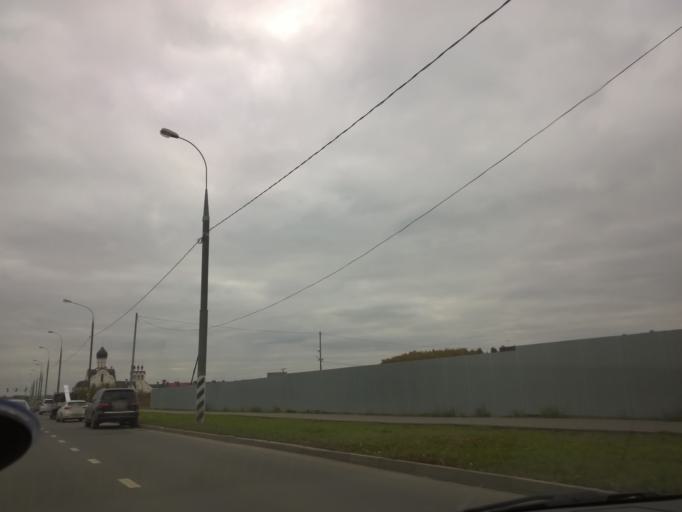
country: RU
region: Moskovskaya
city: Kommunarka
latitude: 55.5342
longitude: 37.4992
